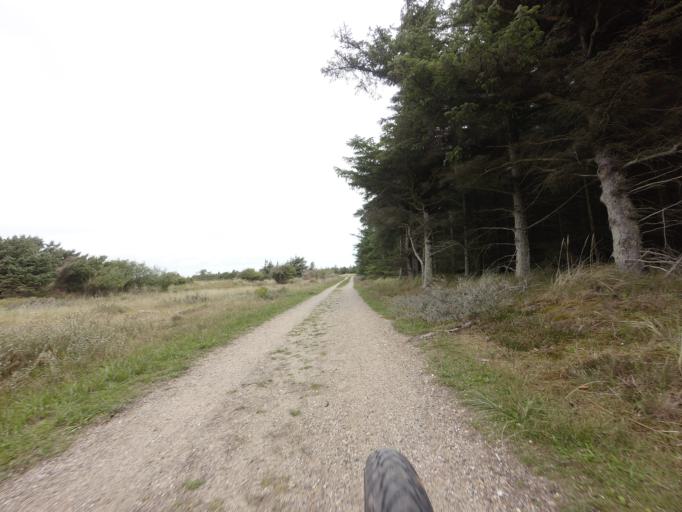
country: DK
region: North Denmark
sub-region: Hjorring Kommune
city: Hirtshals
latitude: 57.5523
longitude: 9.9210
